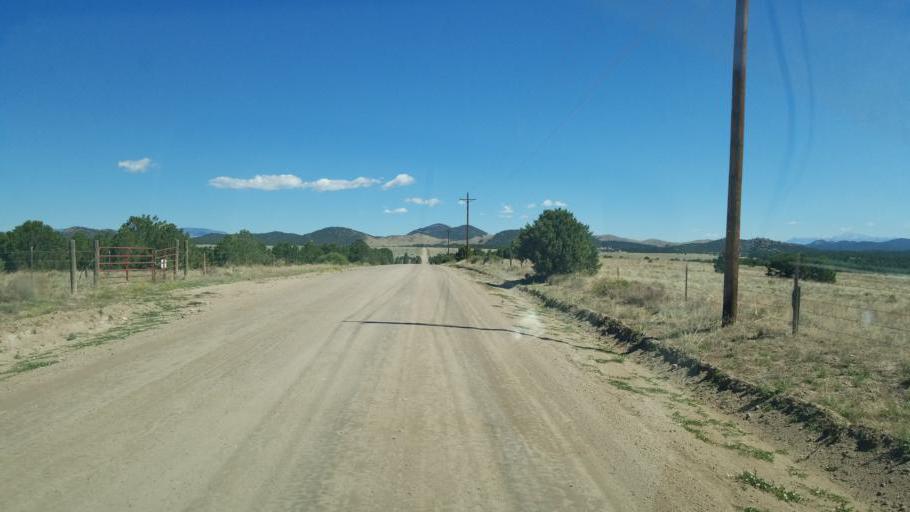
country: US
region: Colorado
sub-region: Custer County
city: Westcliffe
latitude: 38.2679
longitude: -105.5011
